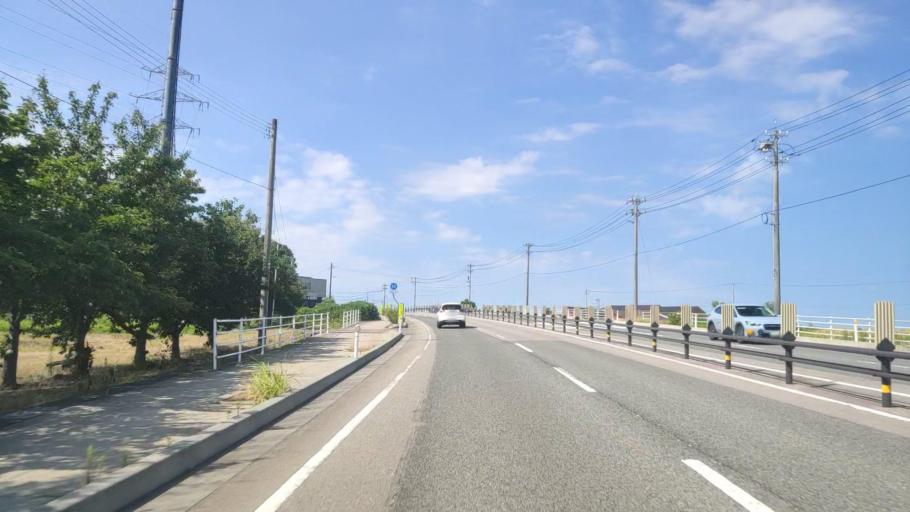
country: JP
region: Ishikawa
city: Komatsu
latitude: 36.4121
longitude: 136.5098
